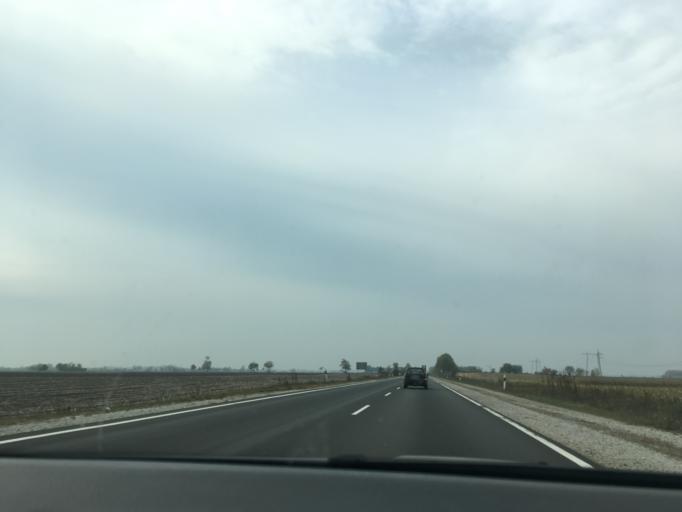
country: HU
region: Pest
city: Abony
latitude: 47.2173
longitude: 20.0333
